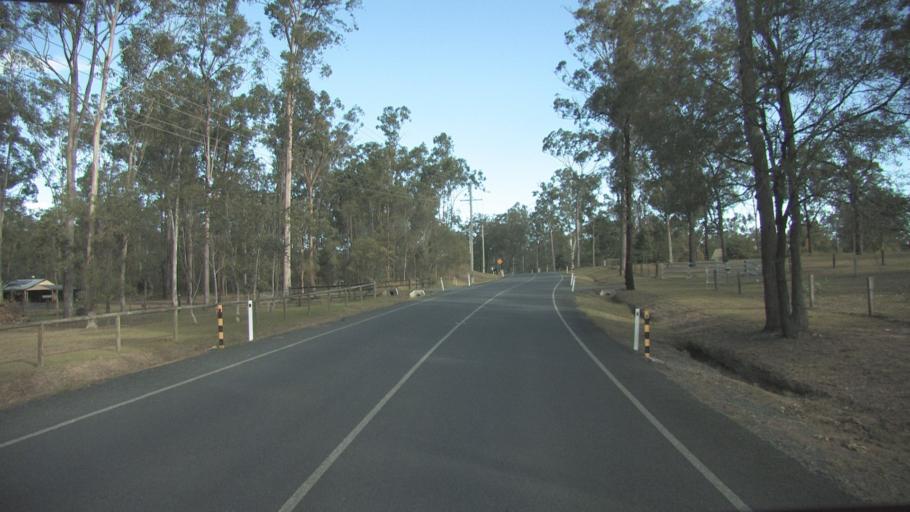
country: AU
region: Queensland
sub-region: Logan
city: North Maclean
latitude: -27.8147
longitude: 153.0564
